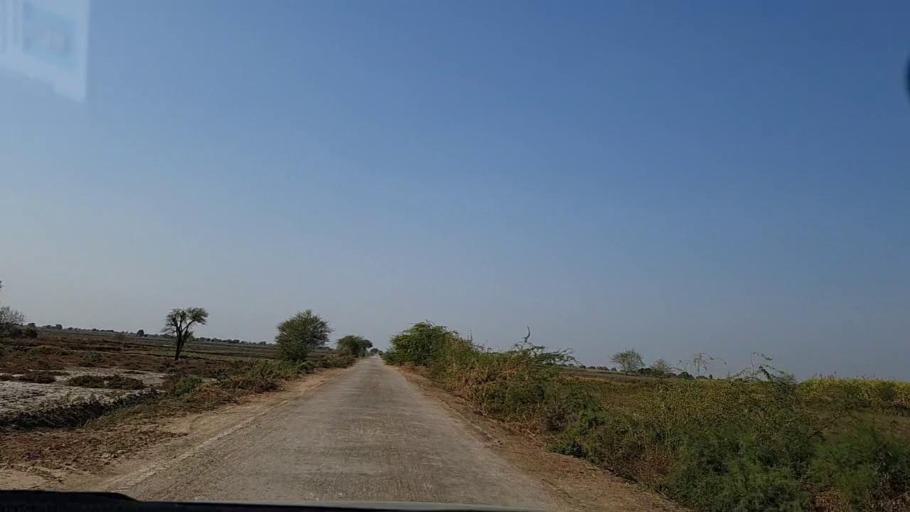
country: PK
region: Sindh
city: Digri
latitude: 25.1667
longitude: 69.0672
